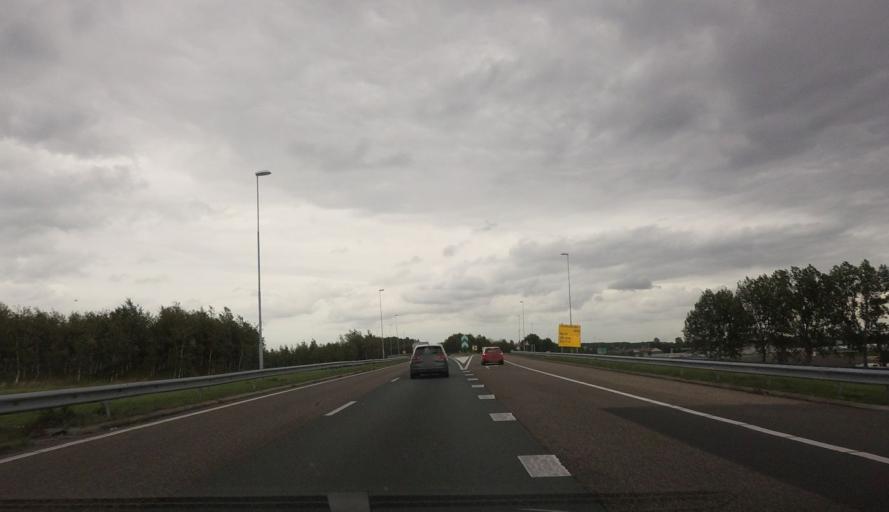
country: NL
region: North Holland
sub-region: Gemeente Haarlemmermeer
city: Hoofddorp
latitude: 52.3537
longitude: 4.7399
